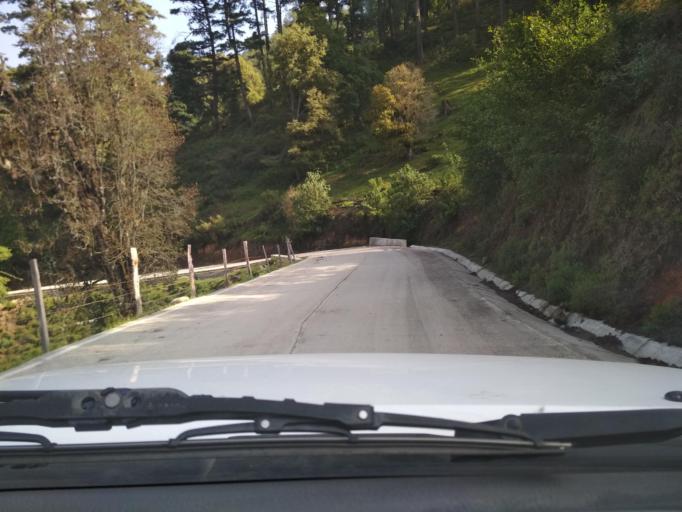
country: MX
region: Veracruz
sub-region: La Perla
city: Chilapa
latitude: 19.0021
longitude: -97.1771
